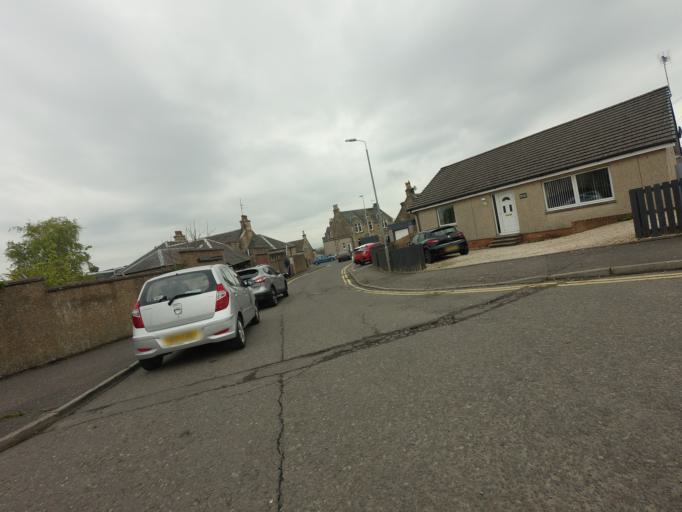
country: GB
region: Scotland
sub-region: Falkirk
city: Polmont
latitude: 55.9809
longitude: -3.7212
